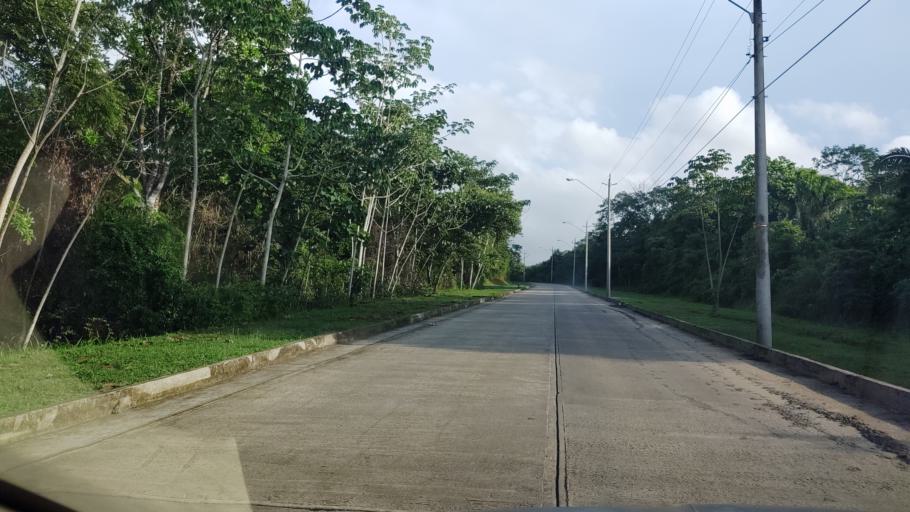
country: PA
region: Panama
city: Nuevo Arraijan
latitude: 8.9216
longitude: -79.7505
